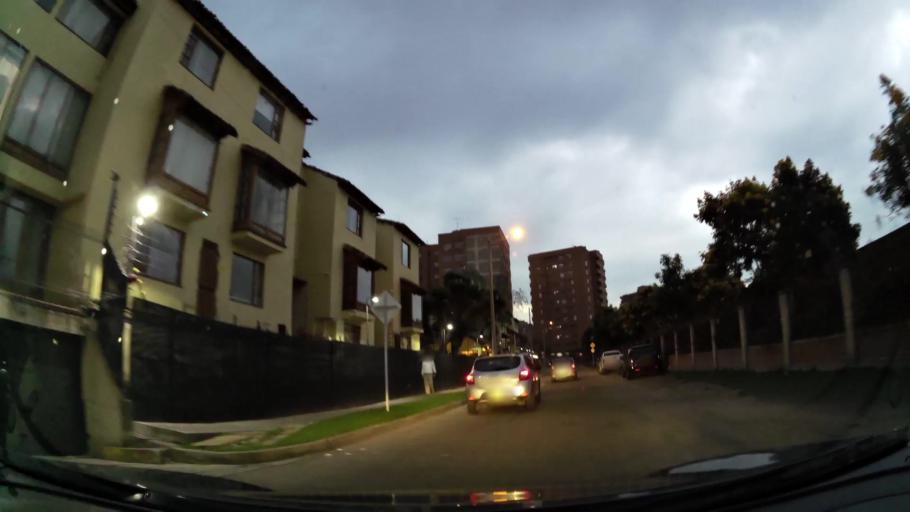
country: CO
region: Bogota D.C.
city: Barrio San Luis
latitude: 4.7142
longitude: -74.0490
